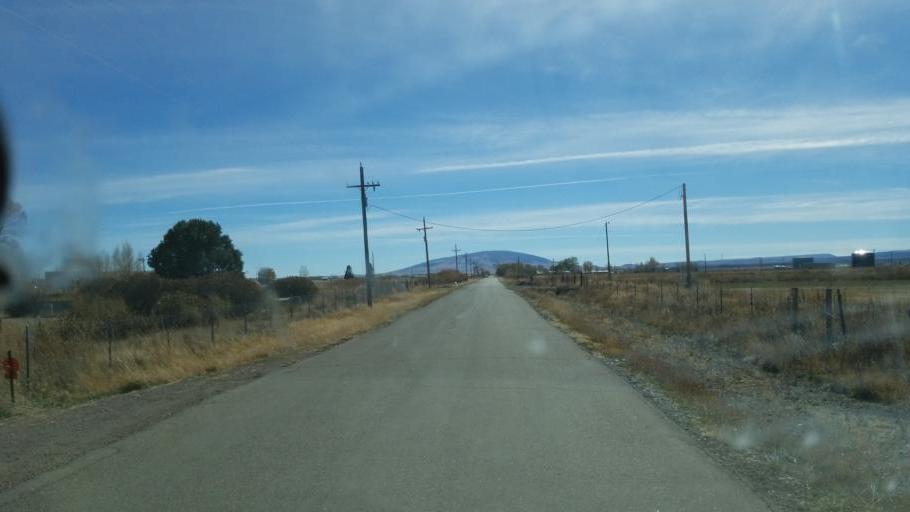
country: US
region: Colorado
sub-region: Conejos County
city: Conejos
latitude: 37.0838
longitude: -106.0194
